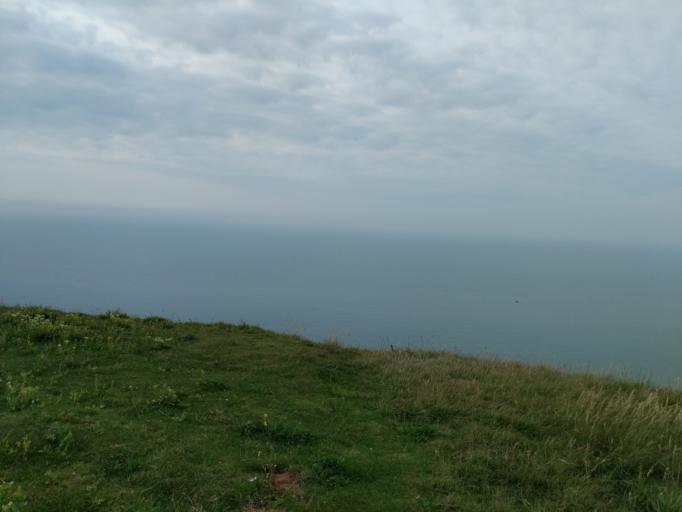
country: GB
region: England
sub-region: Kent
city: Folkestone
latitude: 51.1015
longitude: 1.2259
